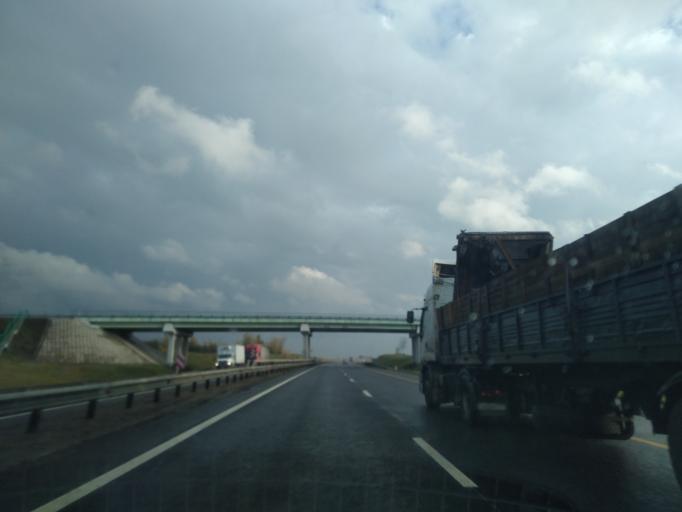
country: RU
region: Lipetsk
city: Yelets
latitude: 52.5642
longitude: 38.7098
